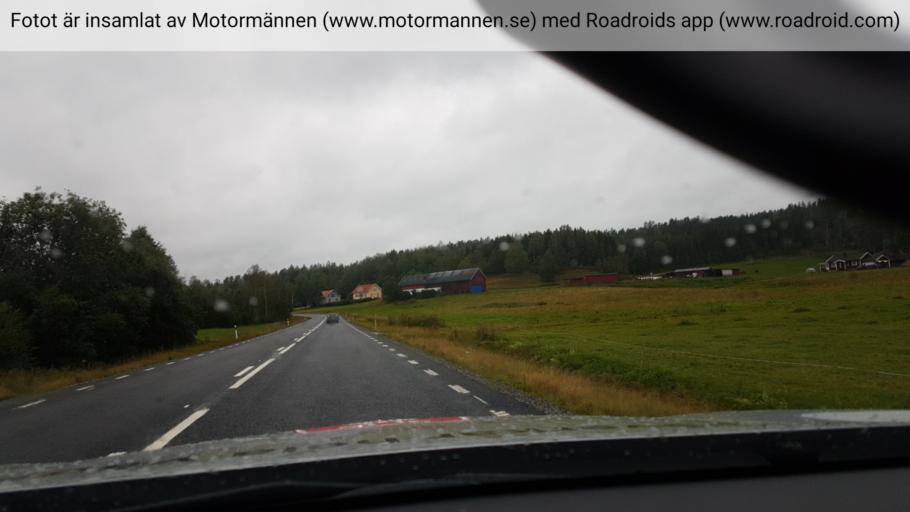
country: SE
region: Vaestra Goetaland
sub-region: Dals-Ed Kommun
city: Ed
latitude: 58.9127
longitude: 12.0121
